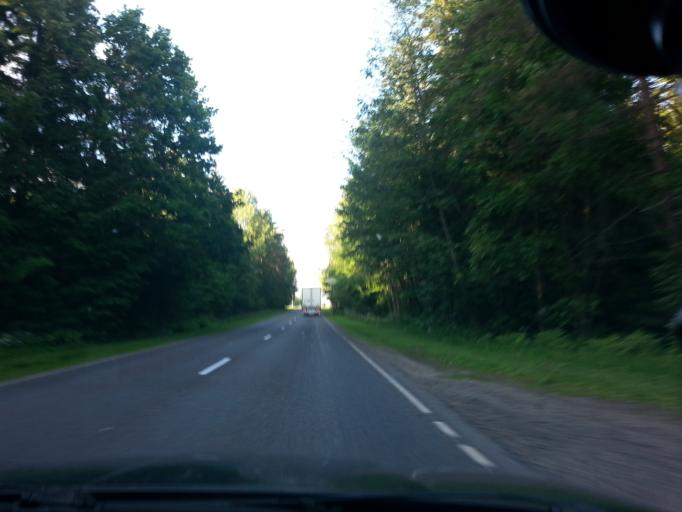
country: BY
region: Minsk
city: Svir
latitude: 54.9113
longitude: 26.4394
